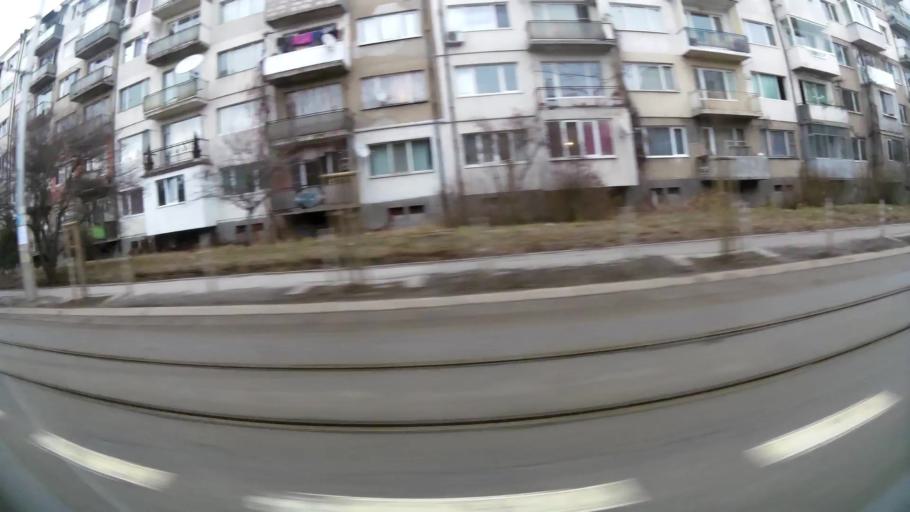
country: BG
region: Sofia-Capital
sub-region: Stolichna Obshtina
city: Sofia
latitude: 42.7351
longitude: 23.3069
